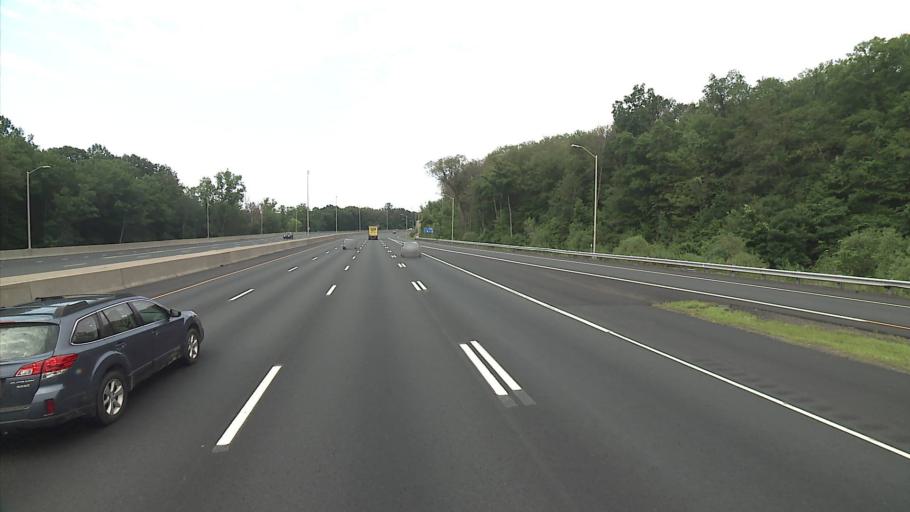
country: US
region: Connecticut
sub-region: New Haven County
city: Prospect
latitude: 41.5395
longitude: -72.9575
